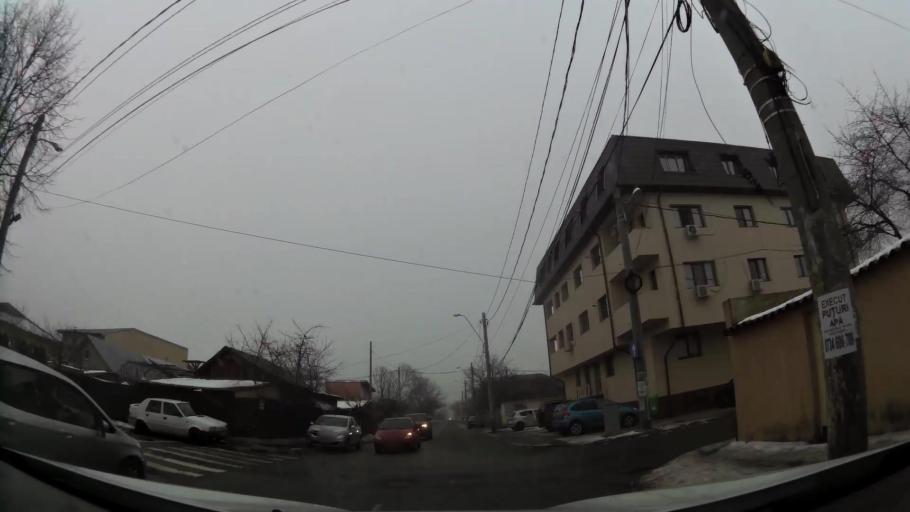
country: RO
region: Ilfov
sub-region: Comuna Chiajna
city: Rosu
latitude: 44.4418
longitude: 26.0103
